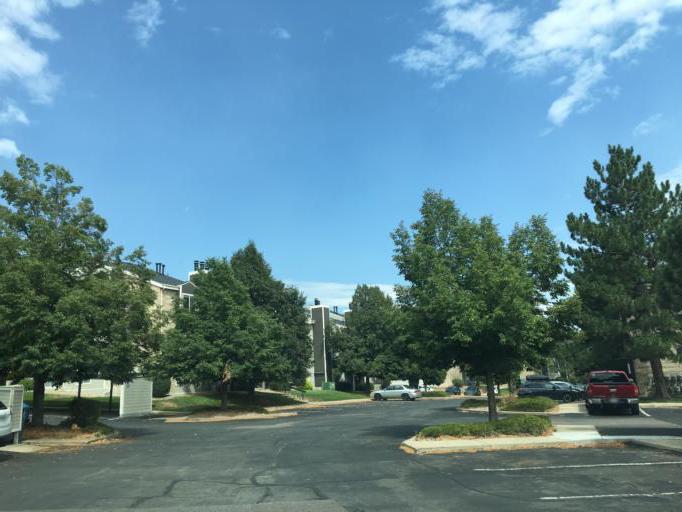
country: US
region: Colorado
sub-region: Jefferson County
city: Applewood
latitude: 39.7442
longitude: -105.1226
